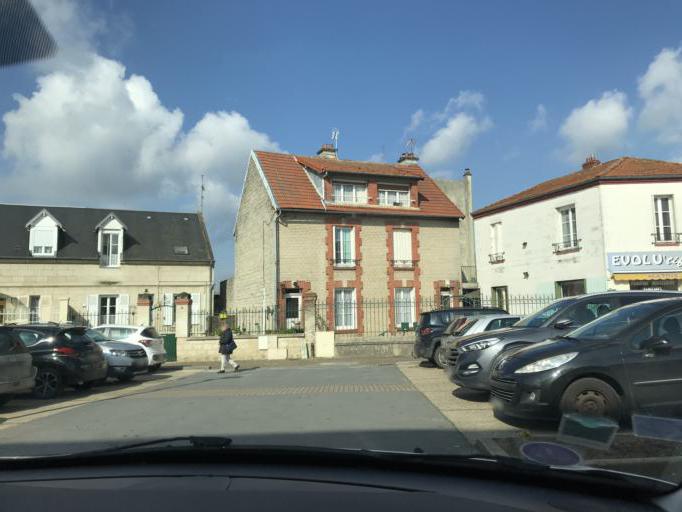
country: FR
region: Picardie
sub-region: Departement de l'Aisne
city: Venizel
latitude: 49.3668
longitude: 3.3947
